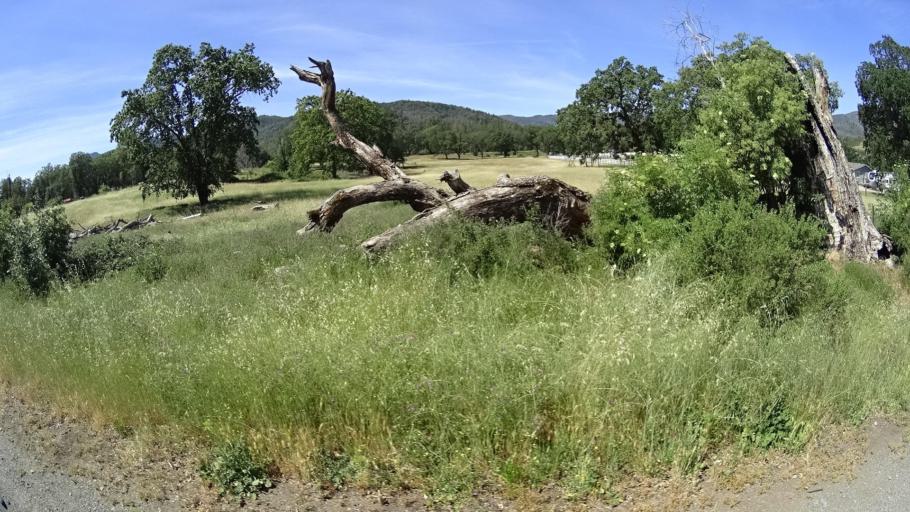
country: US
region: California
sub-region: Lake County
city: Middletown
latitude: 38.7411
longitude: -122.6308
